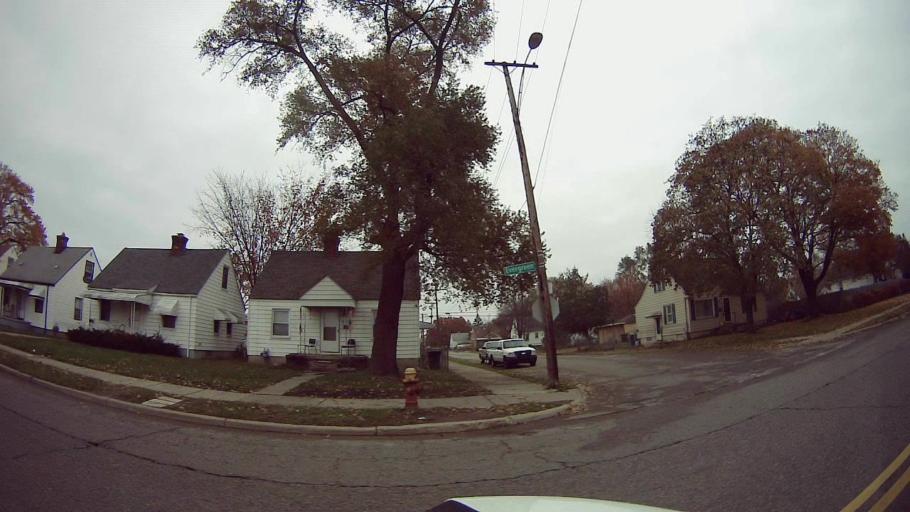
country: US
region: Michigan
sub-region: Wayne County
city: Dearborn Heights
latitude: 42.3344
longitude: -83.2351
